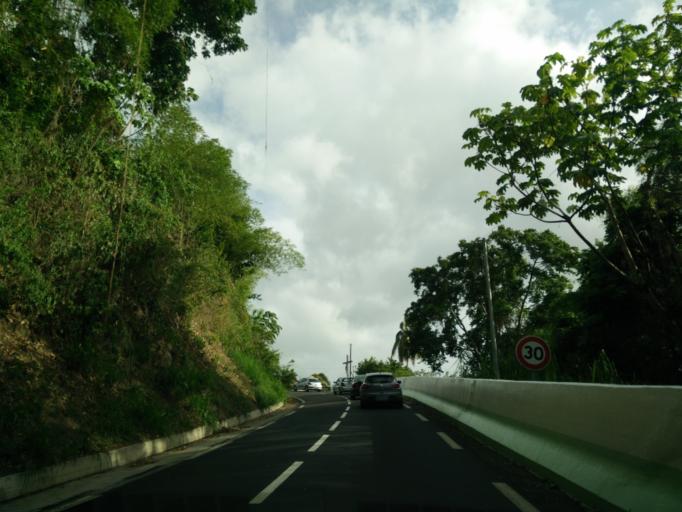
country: MQ
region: Martinique
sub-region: Martinique
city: Saint-Pierre
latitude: 14.7609
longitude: -61.1581
